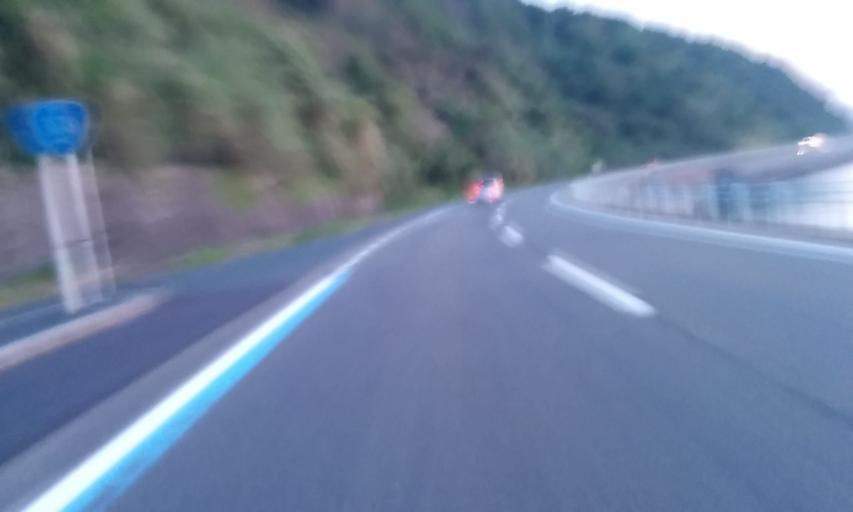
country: JP
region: Ehime
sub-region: Nishiuwa-gun
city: Ikata-cho
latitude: 33.5797
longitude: 132.4466
